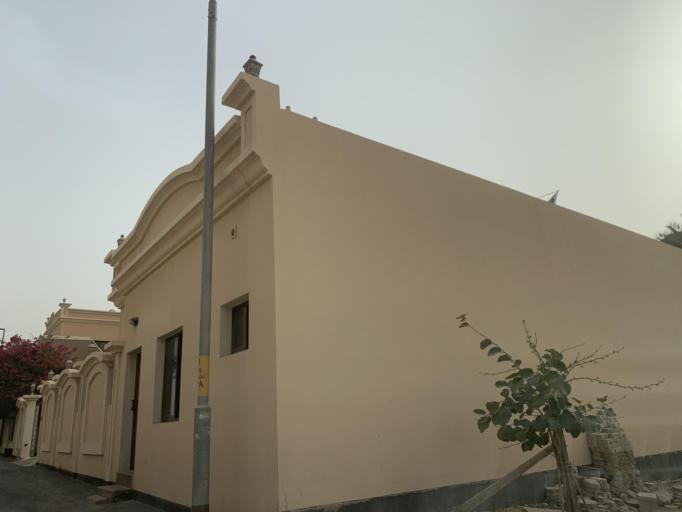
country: BH
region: Northern
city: Ar Rifa'
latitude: 26.1386
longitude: 50.5286
